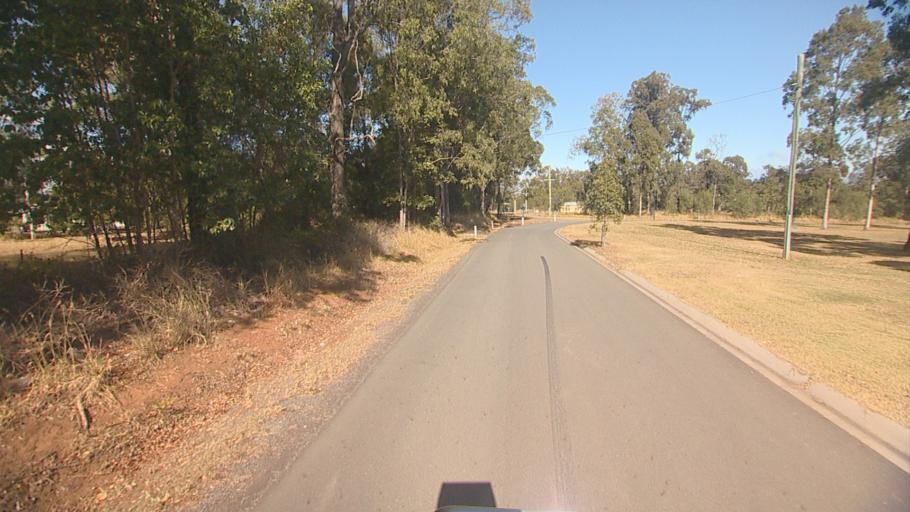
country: AU
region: Queensland
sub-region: Logan
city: Cedar Vale
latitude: -27.8946
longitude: 153.0017
